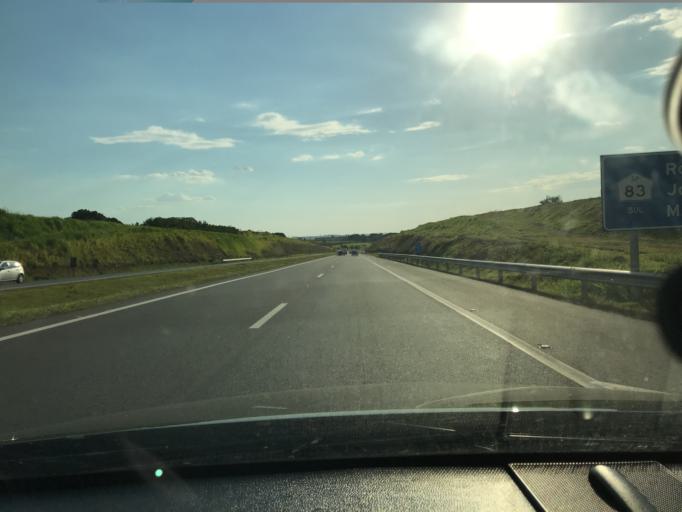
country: BR
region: Sao Paulo
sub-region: Valinhos
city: Valinhos
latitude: -22.9844
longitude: -47.0509
